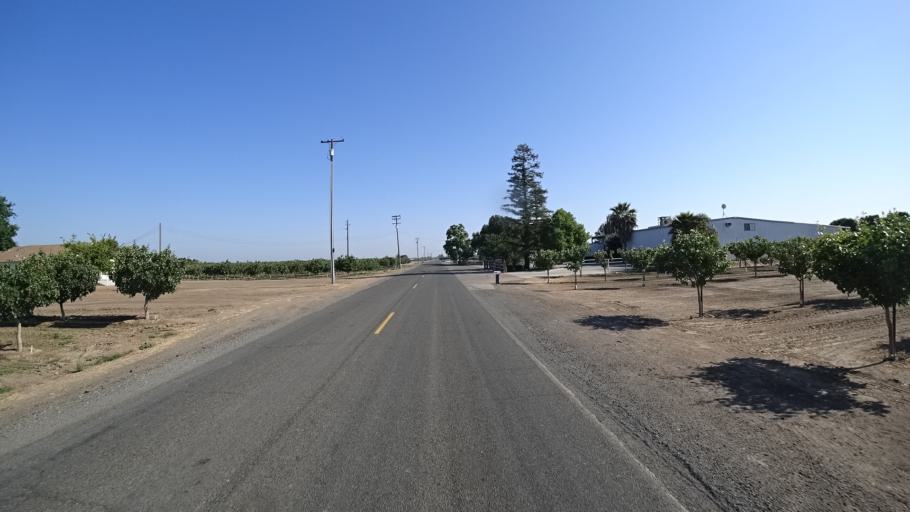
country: US
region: California
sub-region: Kings County
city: Lucerne
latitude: 36.3880
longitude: -119.6911
